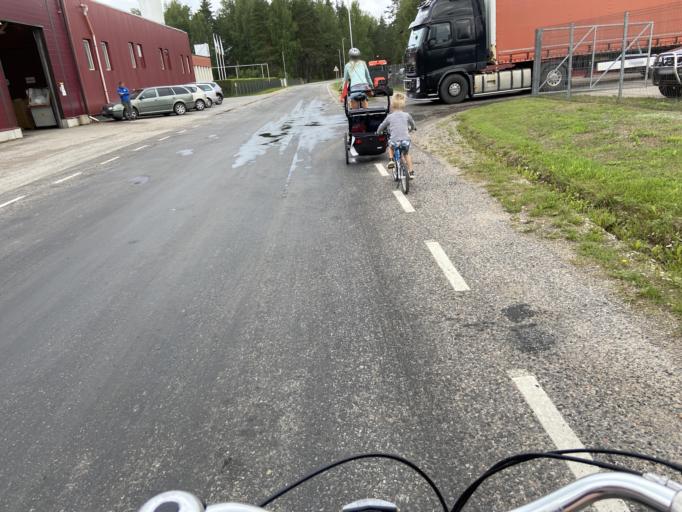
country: RU
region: Pskov
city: Pechory
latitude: 57.9384
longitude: 27.6535
